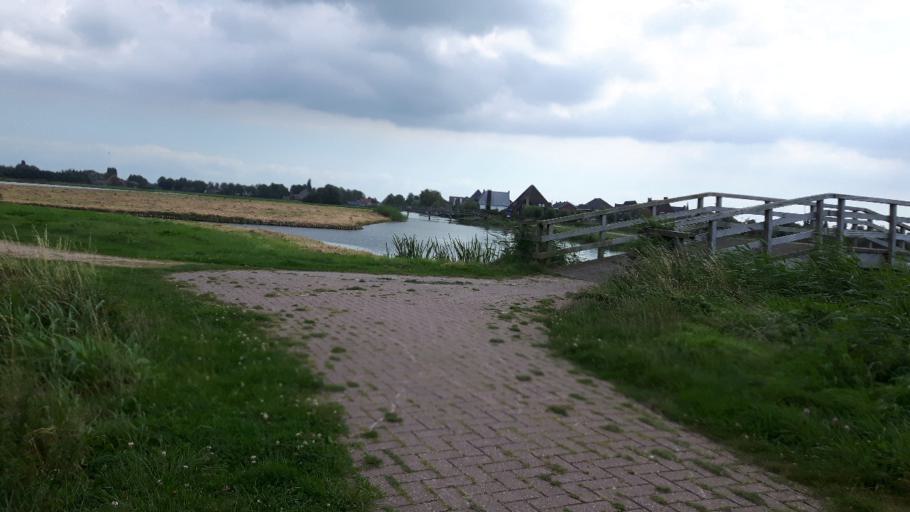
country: NL
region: North Holland
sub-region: Gemeente Medemblik
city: Opperdoes
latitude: 52.7126
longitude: 5.0952
